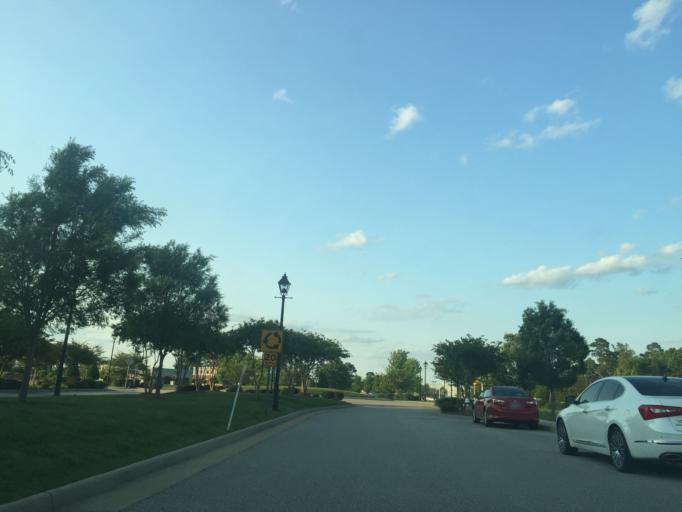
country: US
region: Virginia
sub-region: York County
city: Yorktown
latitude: 37.1117
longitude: -76.5054
